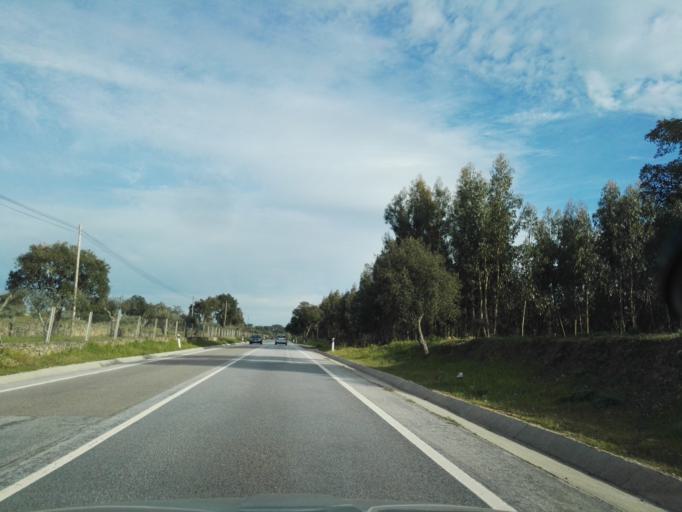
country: PT
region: Portalegre
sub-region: Portalegre
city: Alagoa
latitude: 39.3653
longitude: -7.5557
